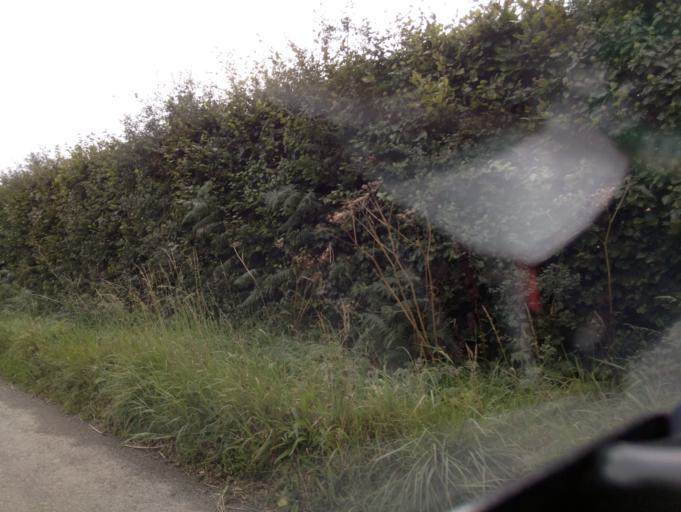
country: GB
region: England
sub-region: Devon
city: Kingsbridge
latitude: 50.2711
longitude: -3.7334
